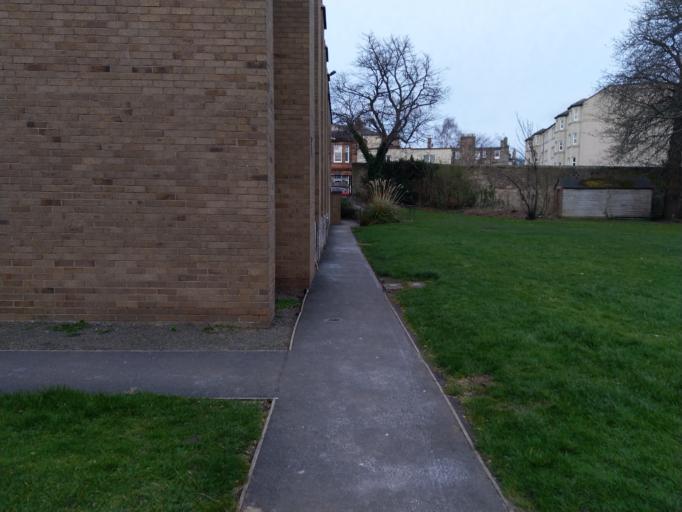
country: GB
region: Scotland
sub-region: Edinburgh
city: Edinburgh
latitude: 55.9267
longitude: -3.2136
